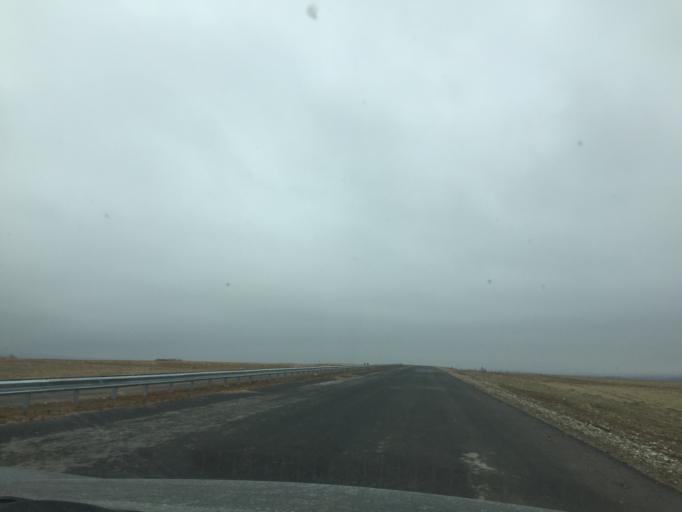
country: KZ
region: Ongtustik Qazaqstan
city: Kokterek
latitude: 42.5421
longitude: 70.2802
